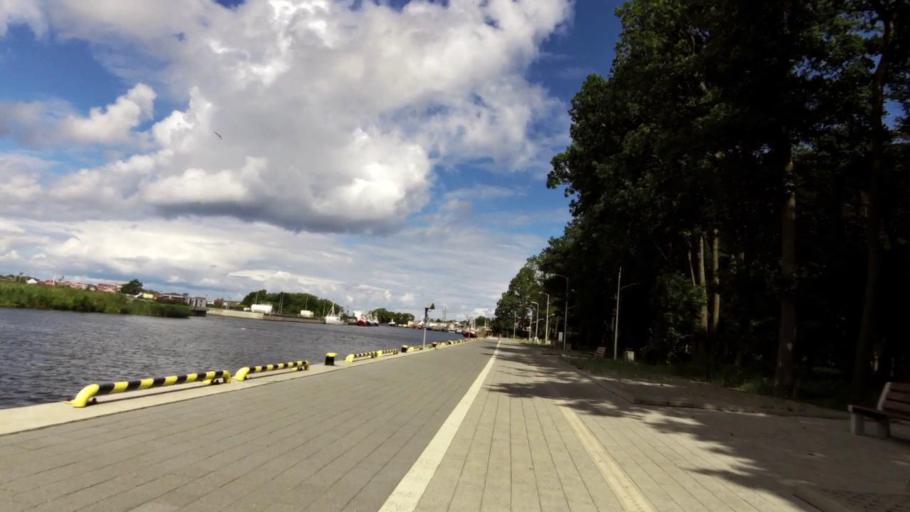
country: PL
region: West Pomeranian Voivodeship
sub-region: Powiat slawienski
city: Darlowo
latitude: 54.4335
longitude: 16.3902
